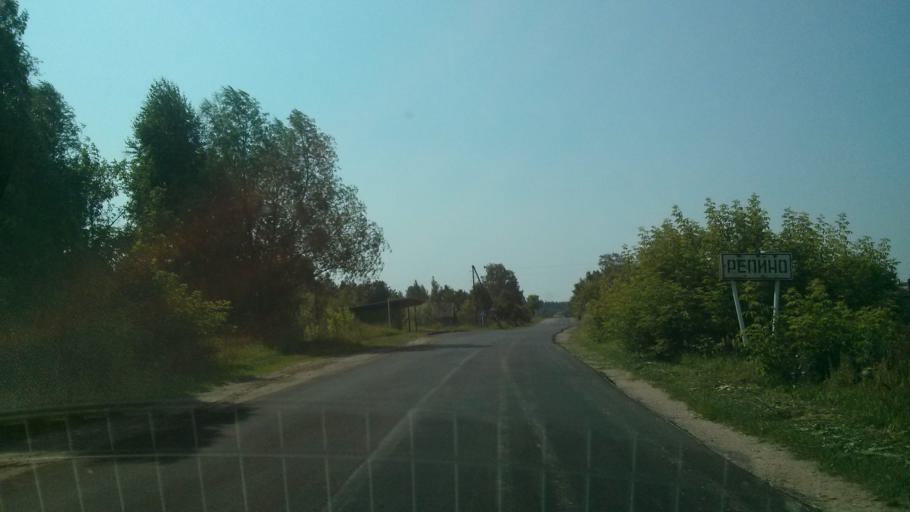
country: RU
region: Vladimir
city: Murom
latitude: 55.4637
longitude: 41.9786
